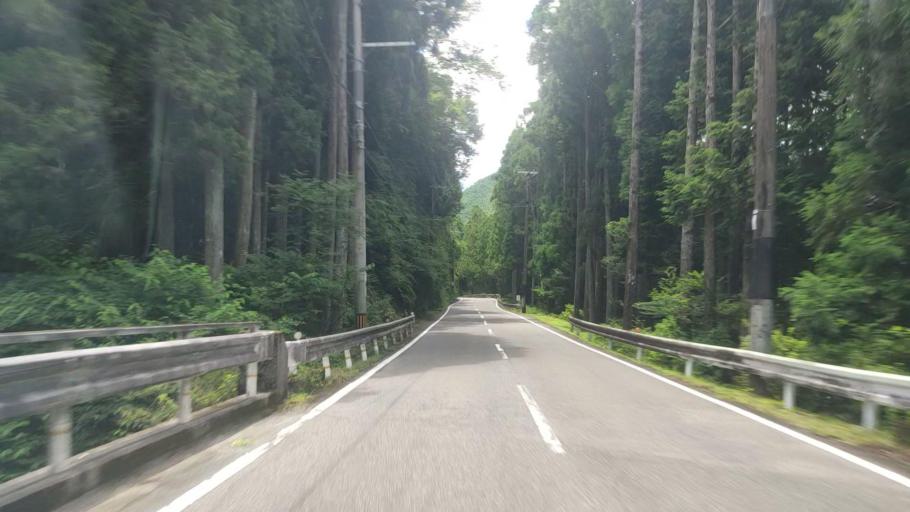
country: JP
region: Mie
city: Owase
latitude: 33.9688
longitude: 136.0617
